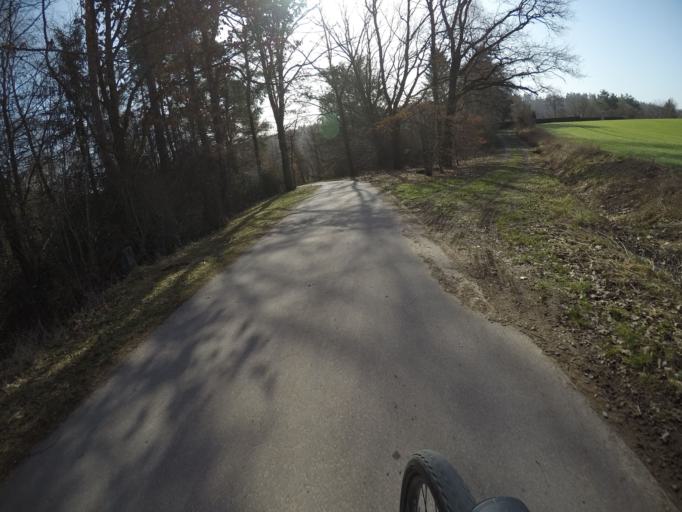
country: DE
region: Baden-Wuerttemberg
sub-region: Regierungsbezirk Stuttgart
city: Schonaich
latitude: 48.6537
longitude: 9.0822
